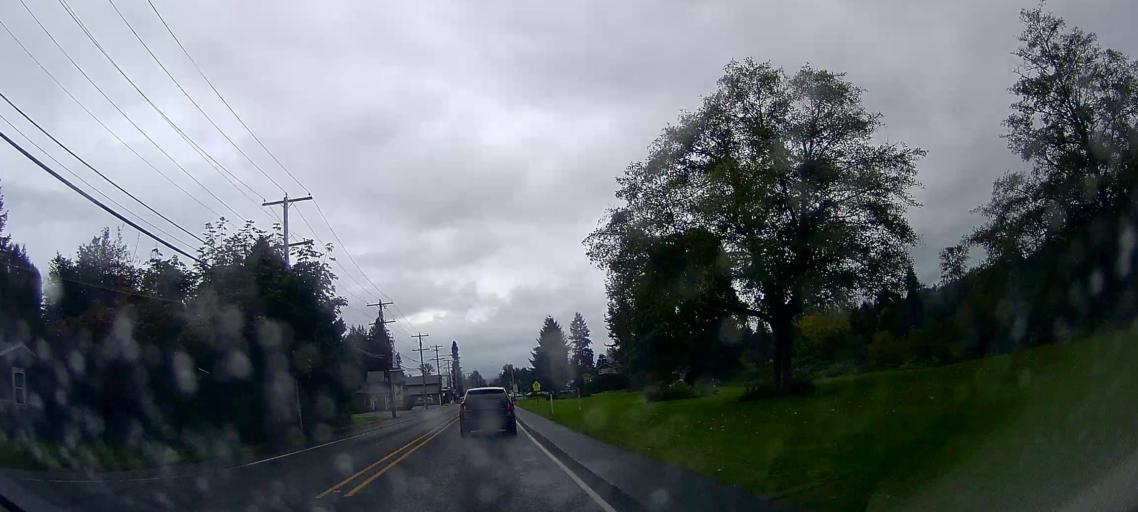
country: US
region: Washington
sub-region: Skagit County
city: Clear Lake
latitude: 48.4637
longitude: -122.2327
